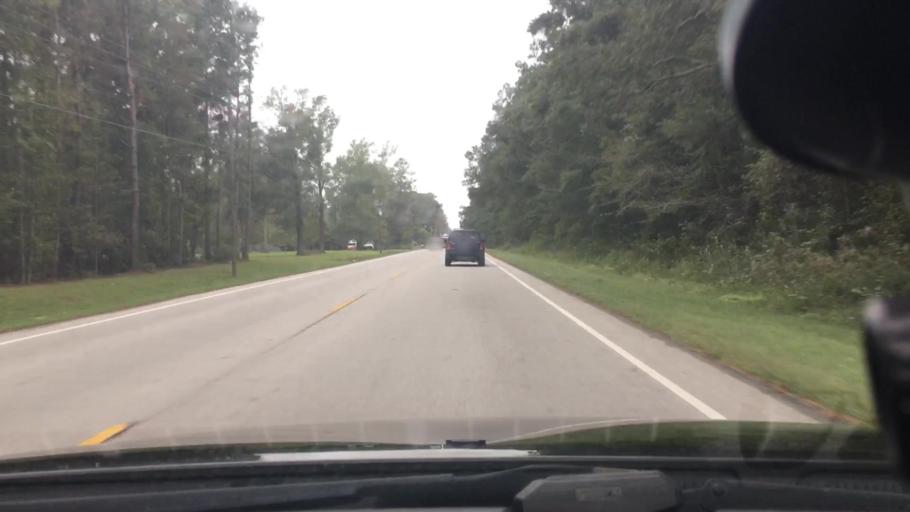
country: US
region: North Carolina
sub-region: Craven County
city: New Bern
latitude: 35.2027
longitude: -77.0577
